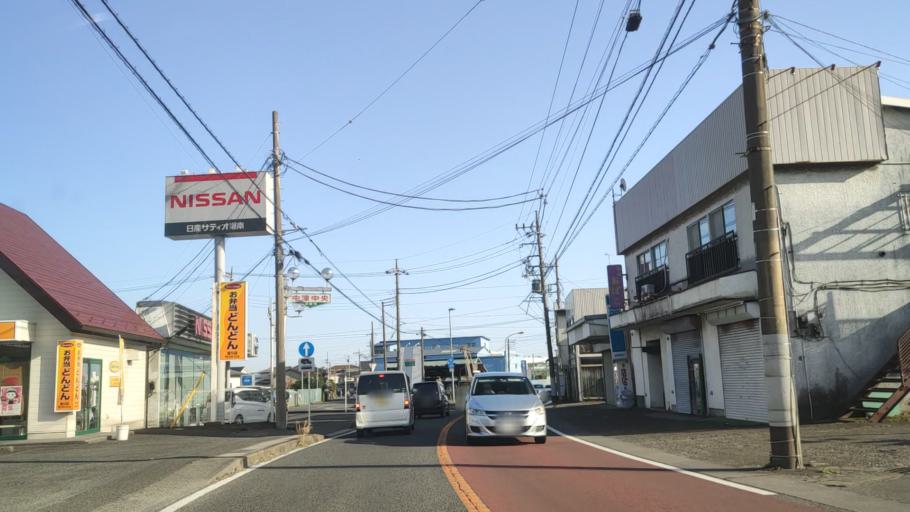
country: JP
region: Kanagawa
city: Zama
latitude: 35.5134
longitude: 139.3374
